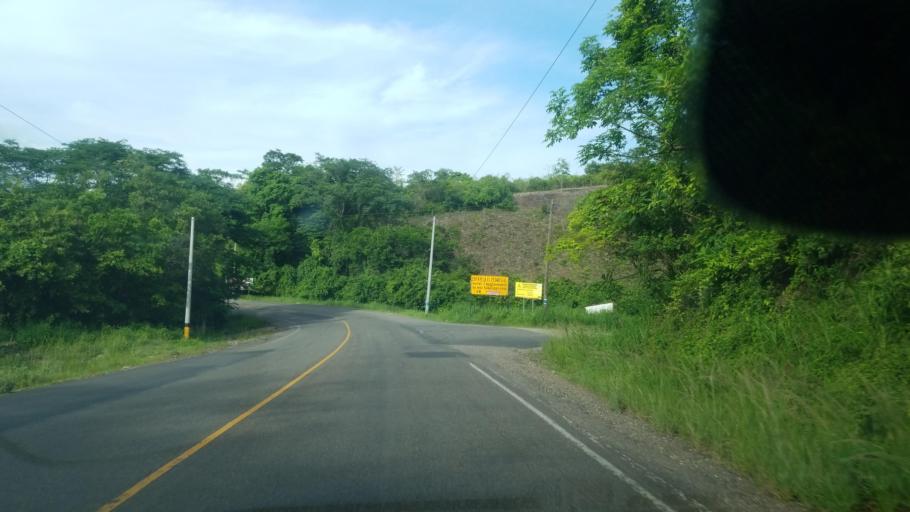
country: HN
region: Santa Barbara
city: Trinidad
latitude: 15.1379
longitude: -88.2429
